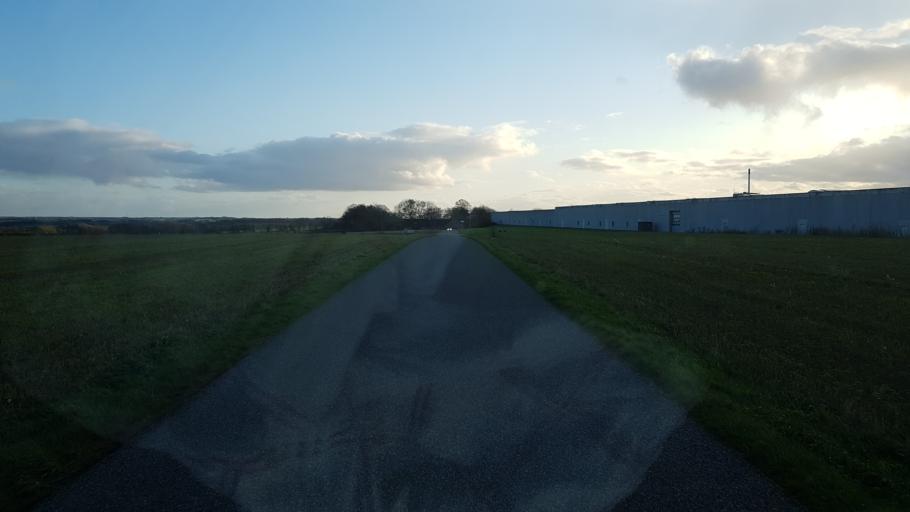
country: DK
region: South Denmark
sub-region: Vejen Kommune
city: Holsted
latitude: 55.4553
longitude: 8.9428
